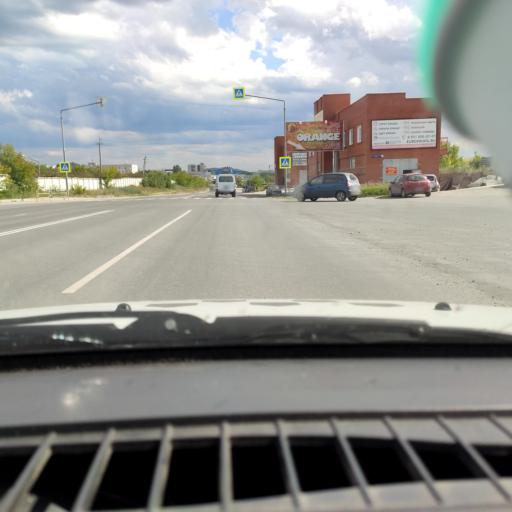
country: RU
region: Chelyabinsk
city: Miass
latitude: 55.0682
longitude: 60.0996
